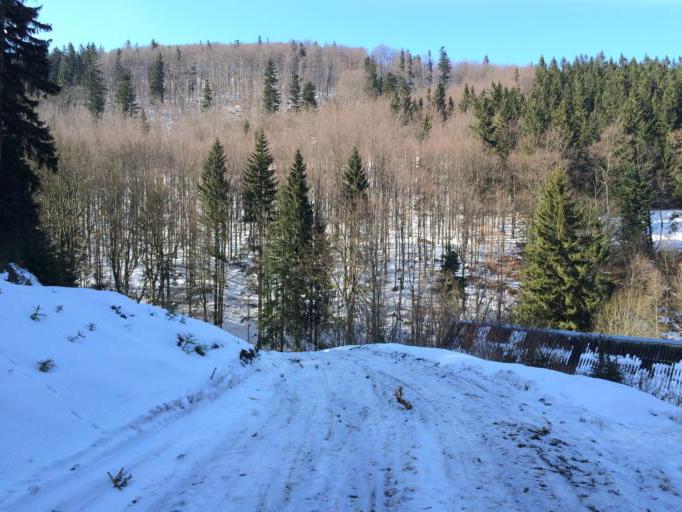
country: CZ
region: Olomoucky
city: Vapenna
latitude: 50.2637
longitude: 16.9961
